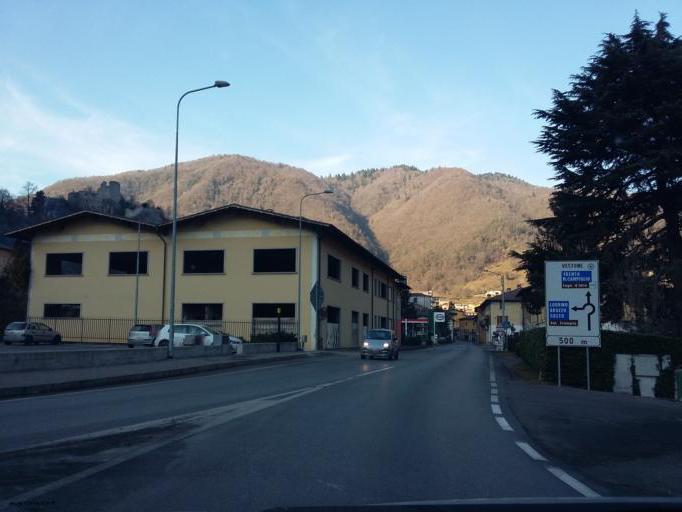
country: IT
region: Lombardy
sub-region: Provincia di Brescia
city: Vestone
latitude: 45.6990
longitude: 10.3884
